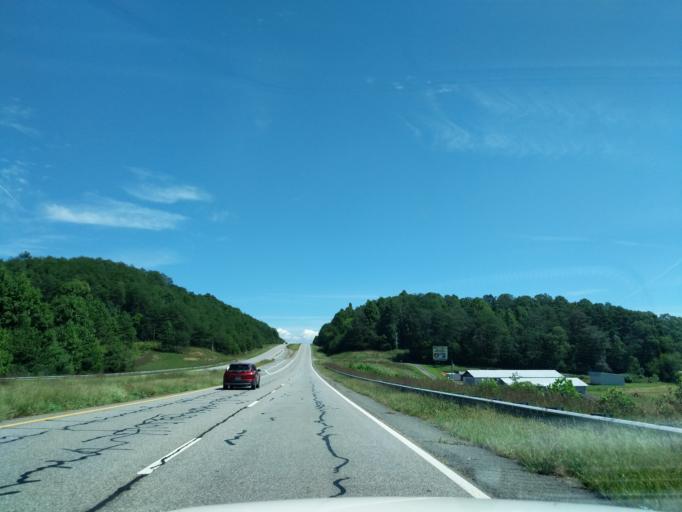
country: US
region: Georgia
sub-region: Fannin County
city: Blue Ridge
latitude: 34.8912
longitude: -84.2387
